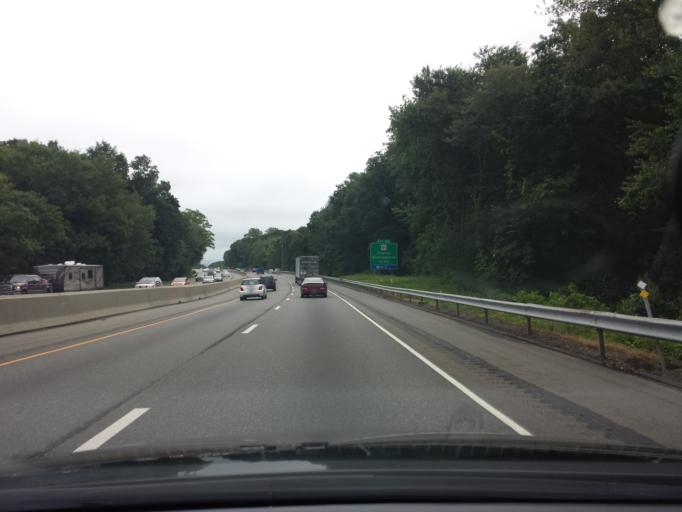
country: US
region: Connecticut
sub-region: Middlesex County
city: Clinton
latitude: 41.2874
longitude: -72.5394
